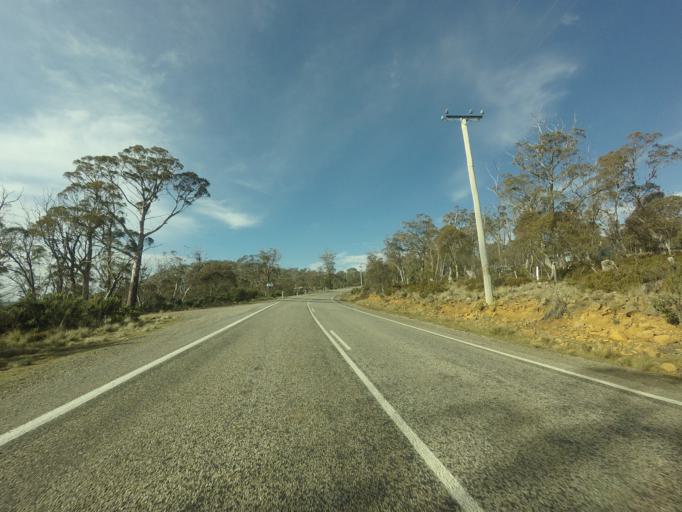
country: AU
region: Tasmania
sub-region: Meander Valley
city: Deloraine
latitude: -41.9904
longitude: 146.6905
